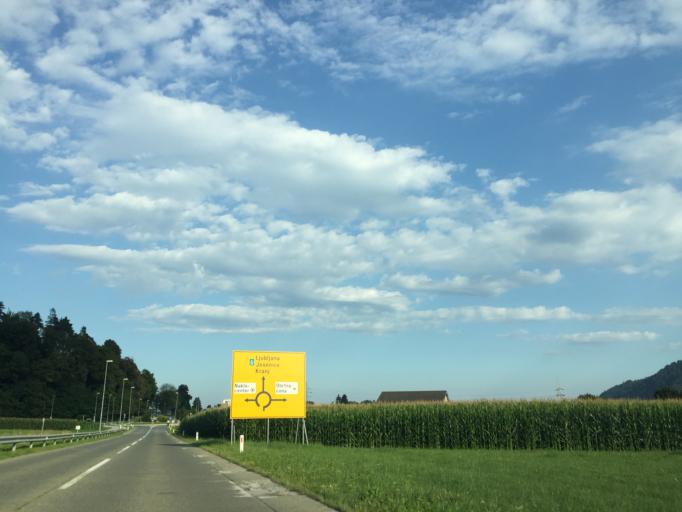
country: SI
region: Naklo
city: Naklo
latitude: 46.2669
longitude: 14.3216
